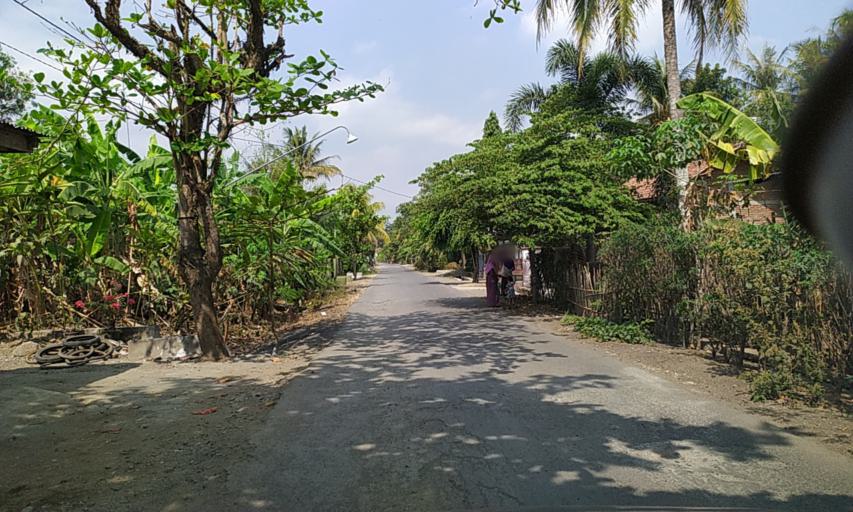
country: ID
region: Central Java
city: Kemantren Satu
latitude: -7.5234
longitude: 108.8882
